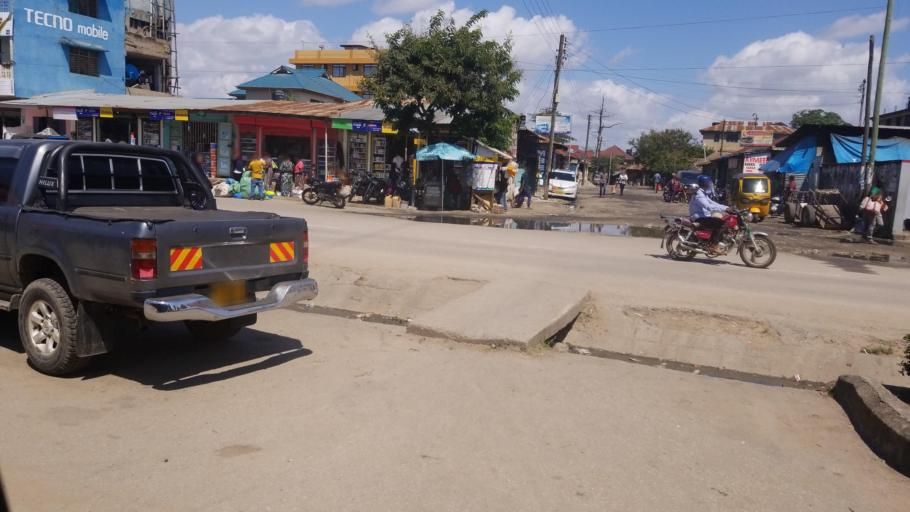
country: TZ
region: Tanga
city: Tanga
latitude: -5.0806
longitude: 39.0981
